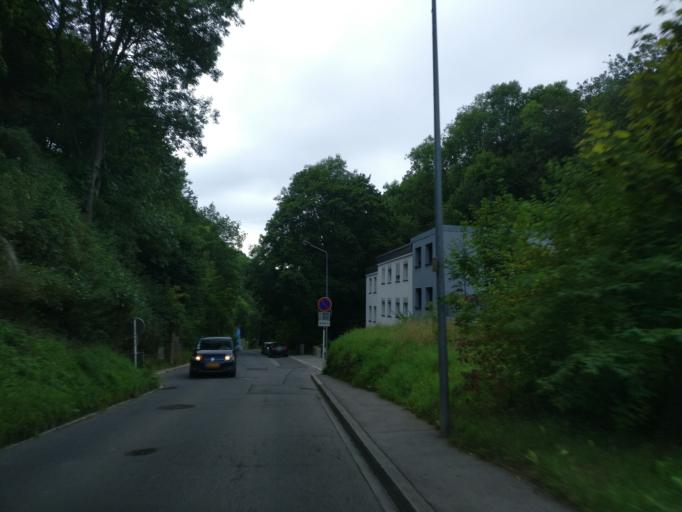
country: LU
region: Luxembourg
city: Kirchberg
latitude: 49.6228
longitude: 6.1387
